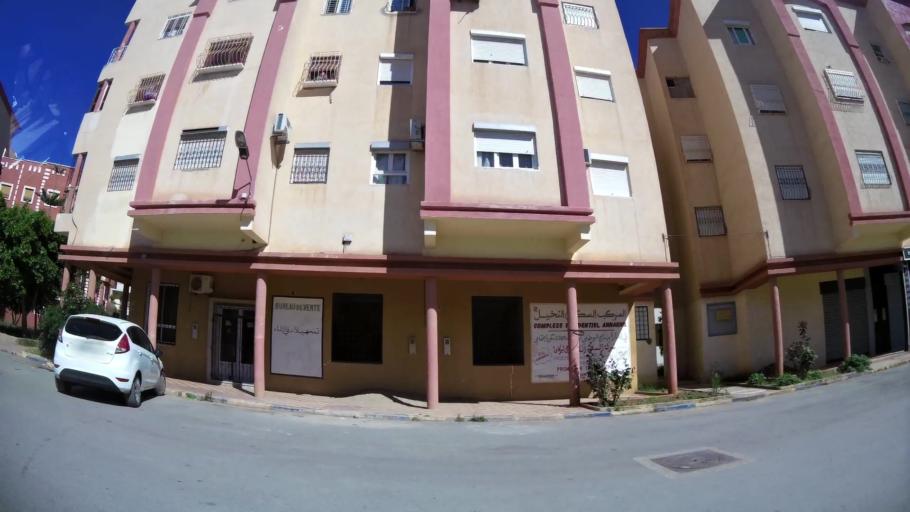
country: MA
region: Oriental
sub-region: Berkane-Taourirt
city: Berkane
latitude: 34.9414
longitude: -2.3310
